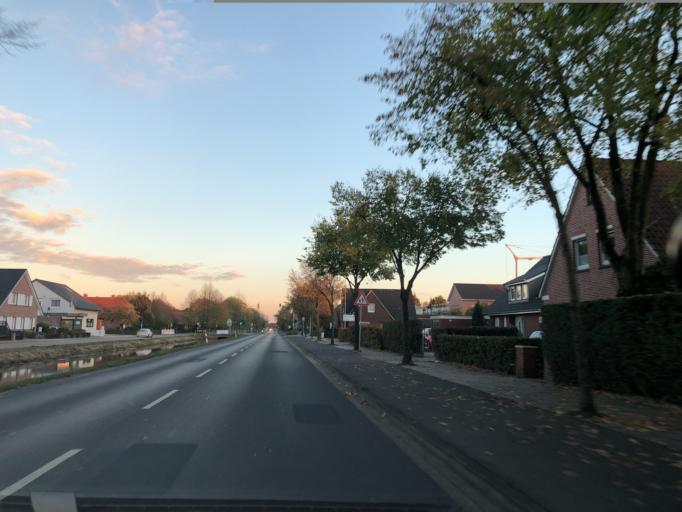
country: DE
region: Lower Saxony
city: Papenburg
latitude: 53.0816
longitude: 7.4168
